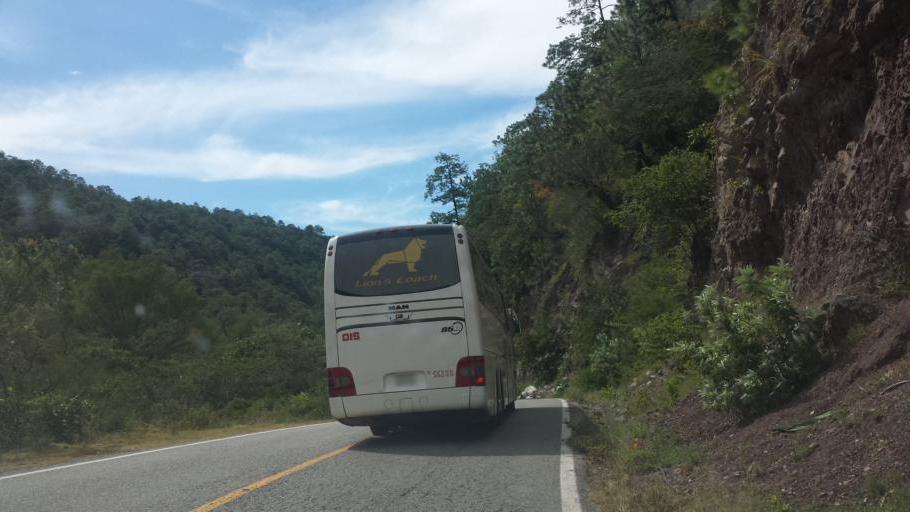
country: MX
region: Oaxaca
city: San Francisco Sola
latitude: 16.4387
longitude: -97.0328
